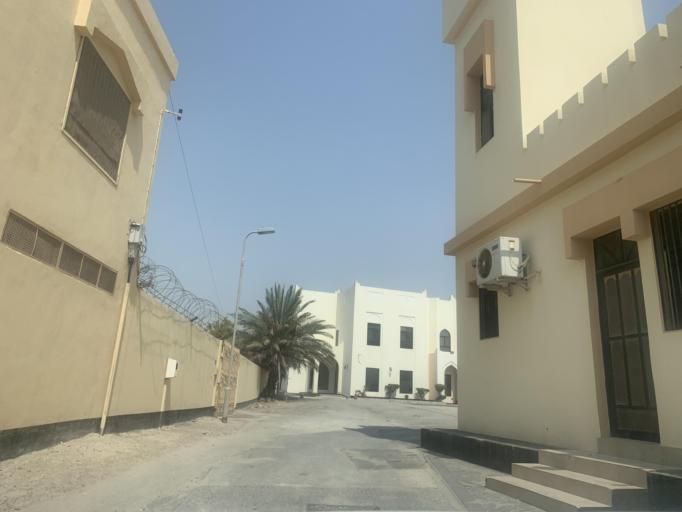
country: BH
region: Central Governorate
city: Madinat Hamad
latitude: 26.1638
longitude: 50.4495
